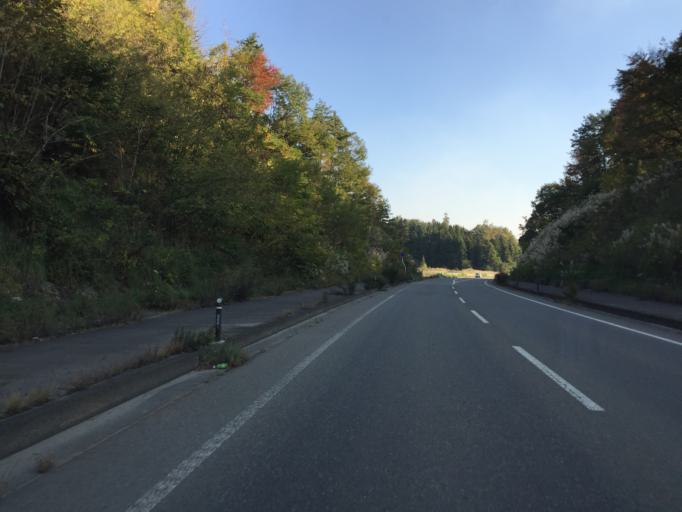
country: JP
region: Fukushima
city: Kitakata
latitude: 37.6944
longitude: 139.8888
